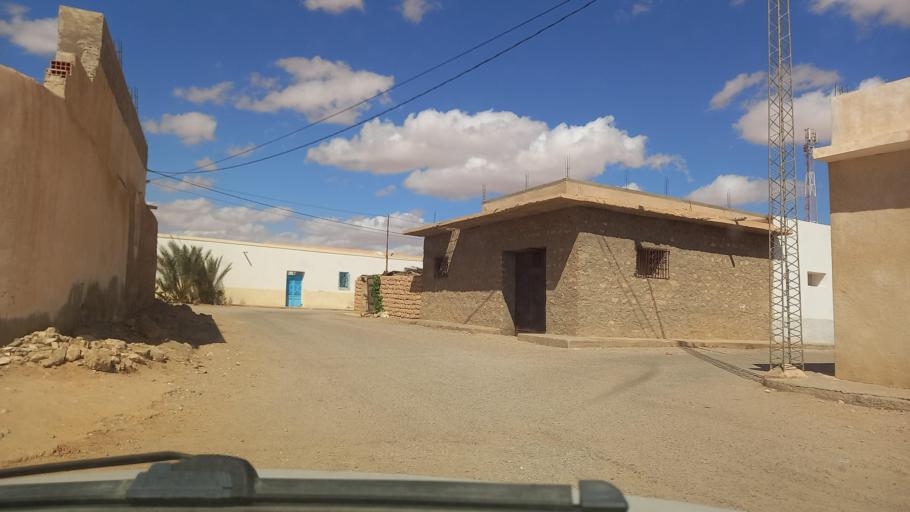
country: TN
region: Tataouine
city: Tataouine
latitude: 32.6953
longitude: 10.3295
